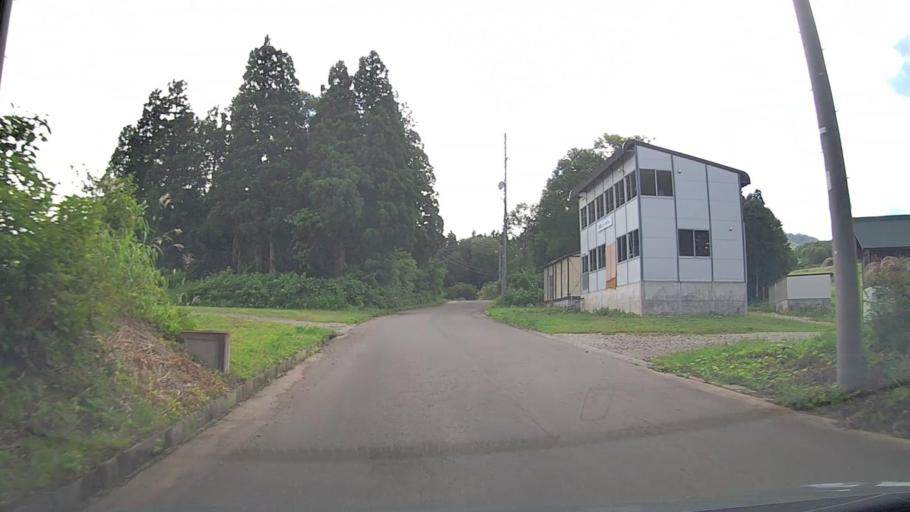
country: JP
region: Nagano
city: Iiyama
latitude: 36.9184
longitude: 138.4819
